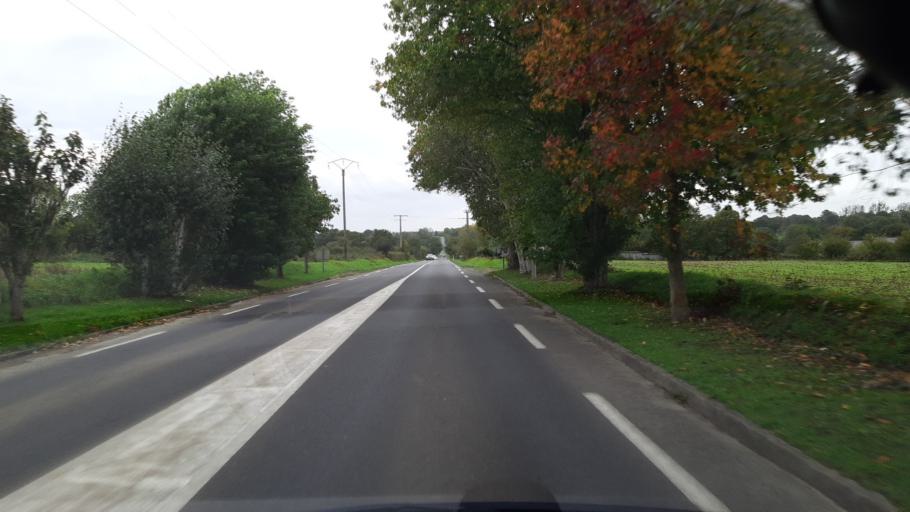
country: FR
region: Lower Normandy
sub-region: Departement de la Manche
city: Hambye
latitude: 48.9465
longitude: -1.2789
